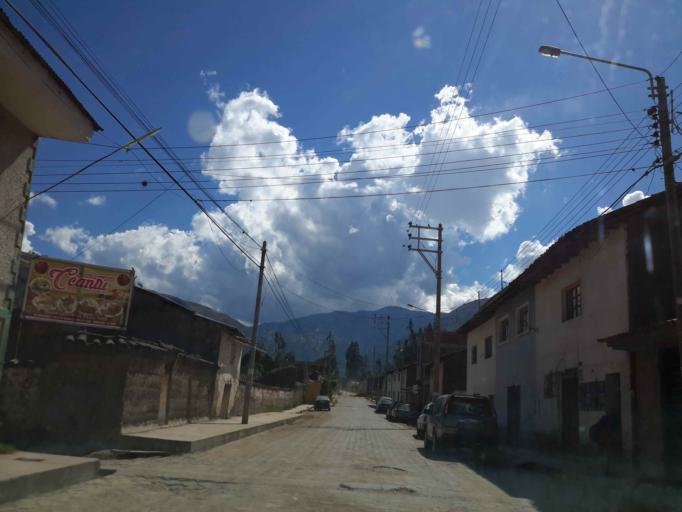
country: PE
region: Apurimac
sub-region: Provincia de Andahuaylas
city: Talavera
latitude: -13.6512
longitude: -73.4349
